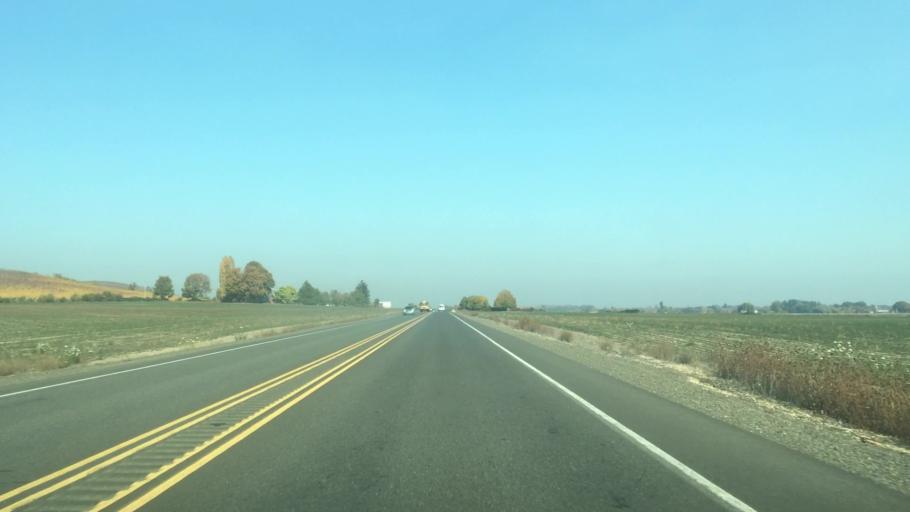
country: US
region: Oregon
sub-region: Yamhill County
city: Amity
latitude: 45.1331
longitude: -123.2950
